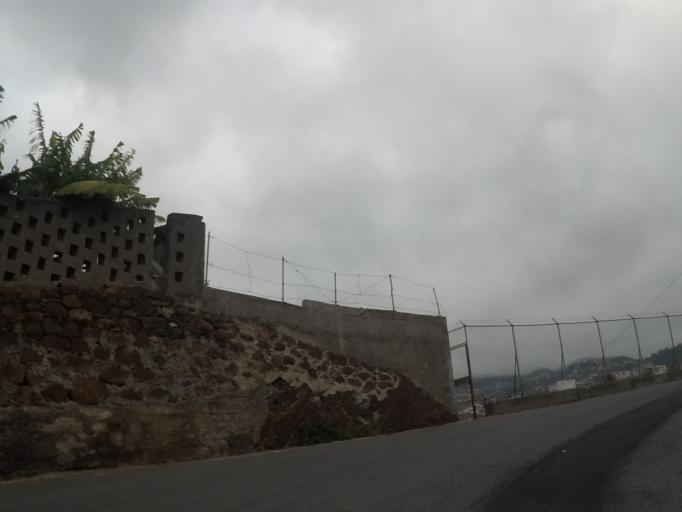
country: PT
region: Madeira
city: Camara de Lobos
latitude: 32.6520
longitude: -16.9744
